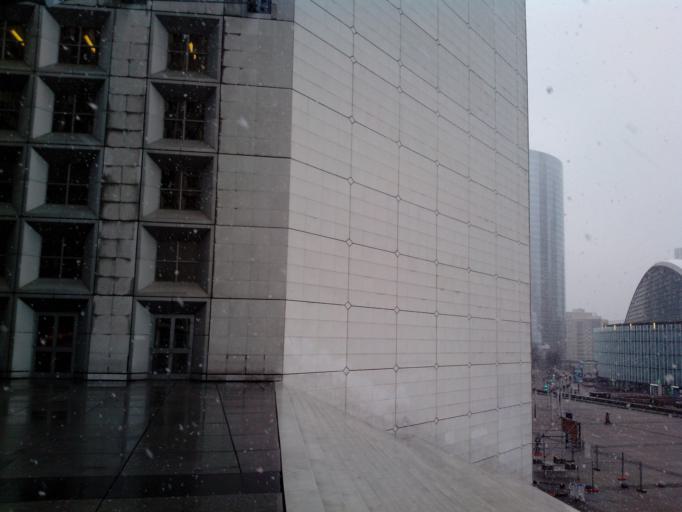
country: FR
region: Ile-de-France
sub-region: Departement des Hauts-de-Seine
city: La Defense
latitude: 48.8925
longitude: 2.2364
